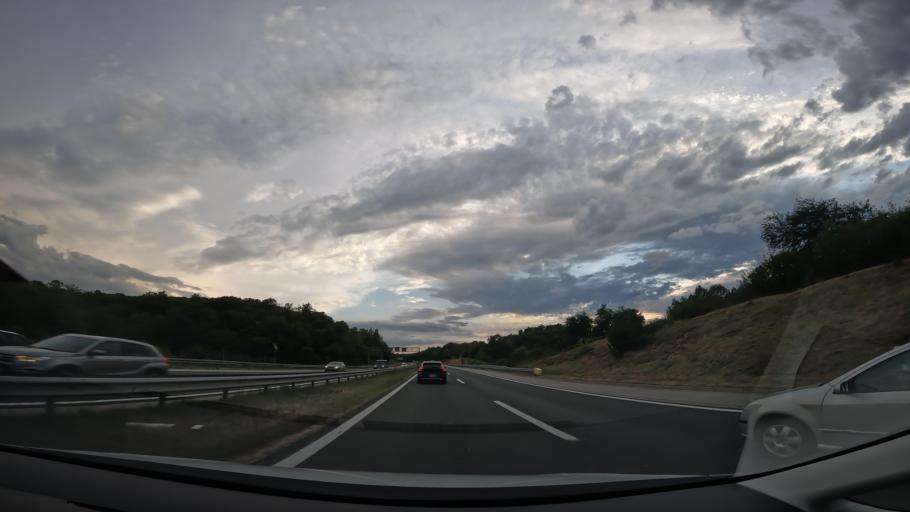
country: HR
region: Karlovacka
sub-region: Grad Karlovac
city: Karlovac
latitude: 45.4844
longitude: 15.4415
